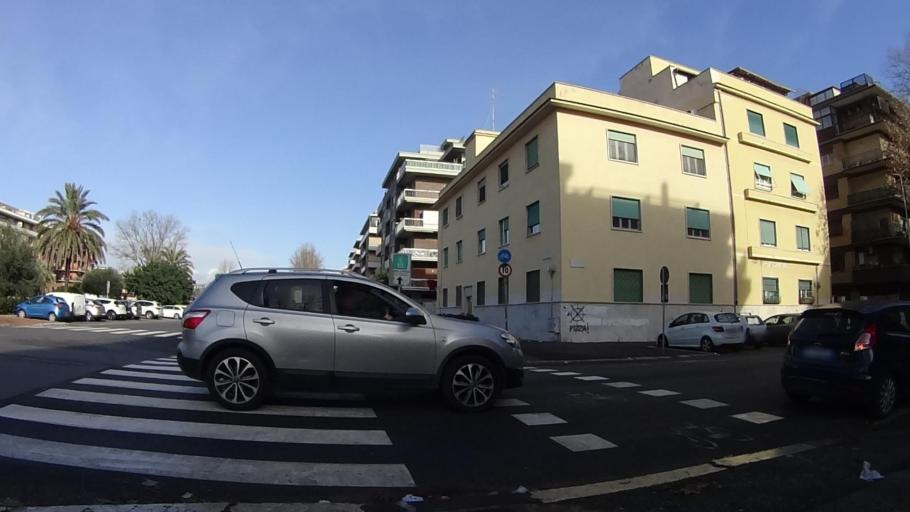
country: IT
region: Latium
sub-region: Citta metropolitana di Roma Capitale
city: Lido di Ostia
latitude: 41.7346
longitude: 12.2680
